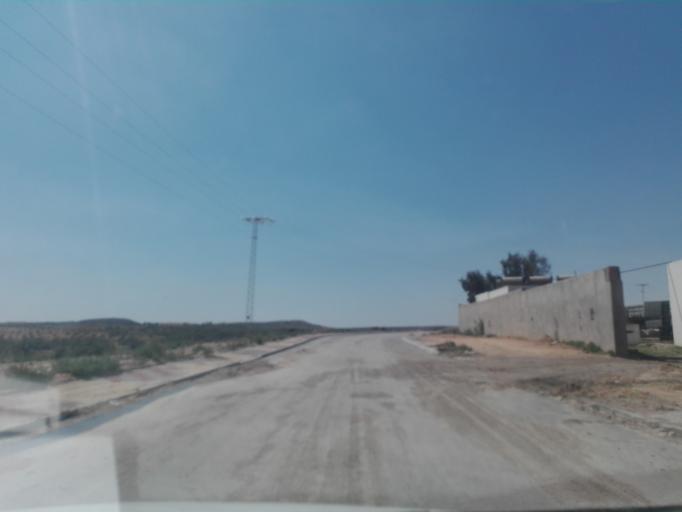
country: TN
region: Safaqis
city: Sfax
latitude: 34.7237
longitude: 10.5227
